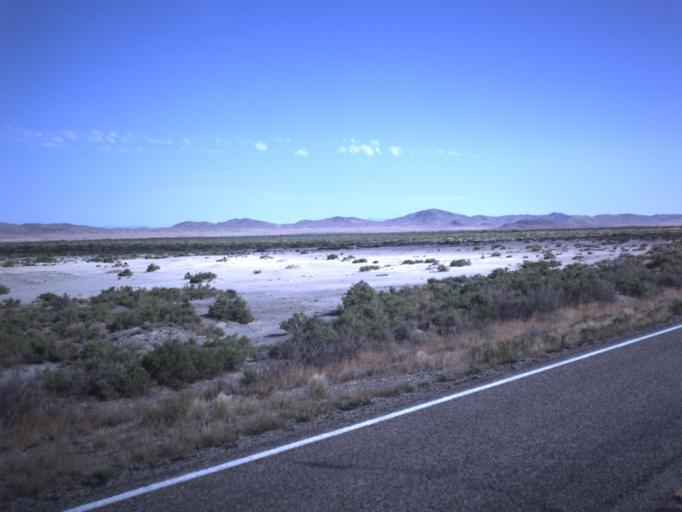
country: US
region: Utah
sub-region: Beaver County
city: Milford
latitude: 38.6100
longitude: -112.9861
